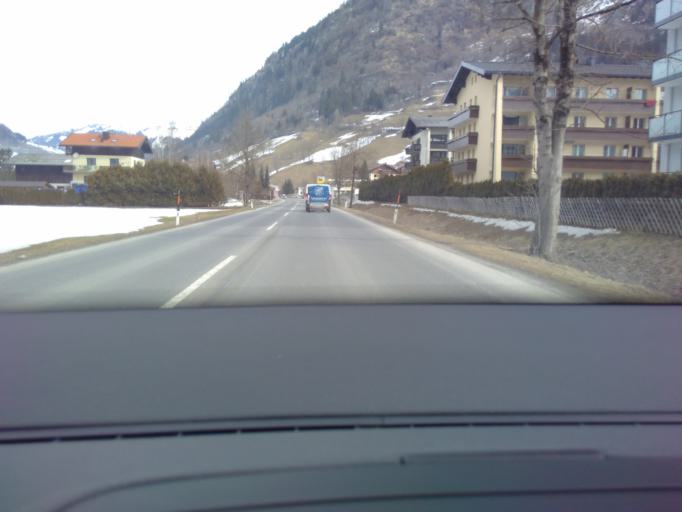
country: AT
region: Salzburg
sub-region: Politischer Bezirk Sankt Johann im Pongau
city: Bad Hofgastein
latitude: 47.1755
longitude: 13.1001
